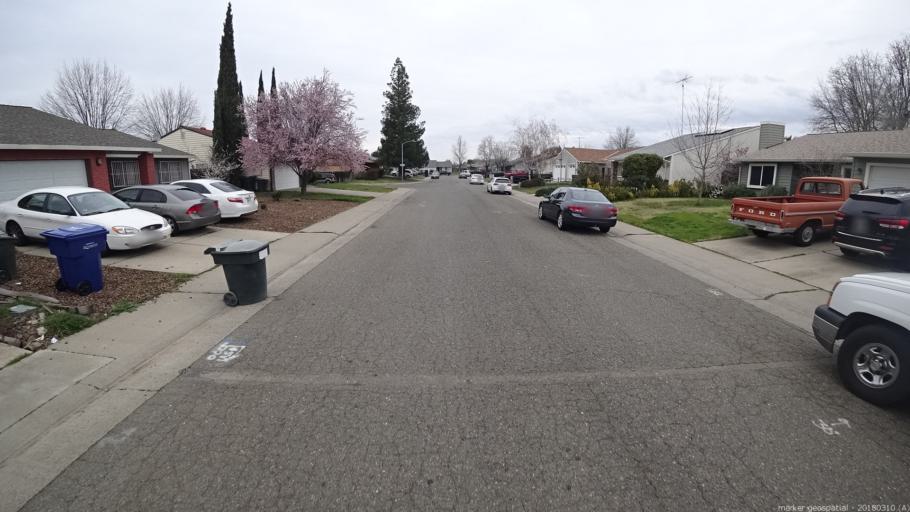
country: US
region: California
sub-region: Sacramento County
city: Vineyard
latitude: 38.4764
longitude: -121.3792
